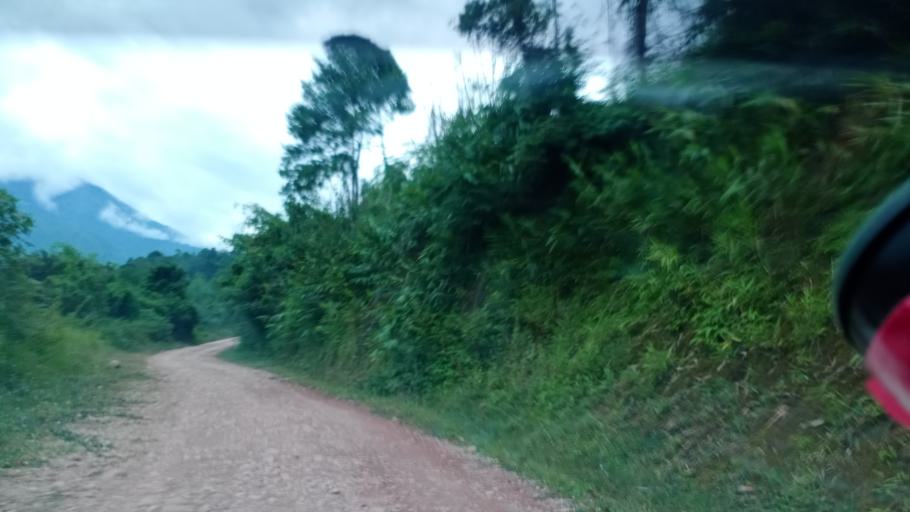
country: TH
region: Changwat Bueng Kan
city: Pak Khat
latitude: 18.7147
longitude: 103.2198
